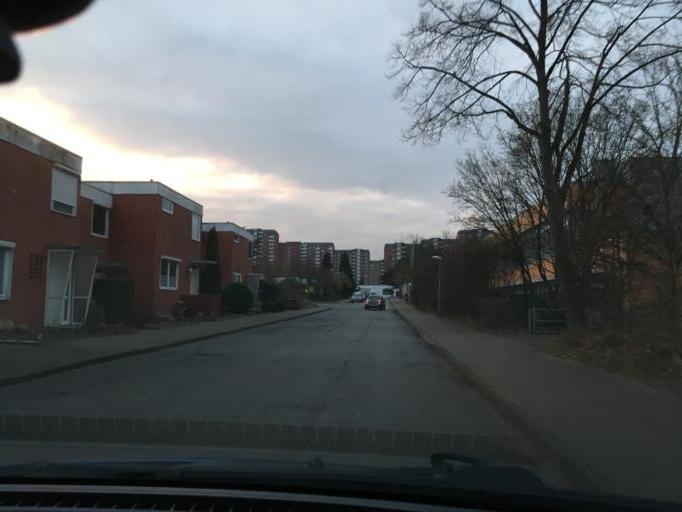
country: DE
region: Lower Saxony
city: Lueneburg
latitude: 53.2390
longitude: 10.4386
